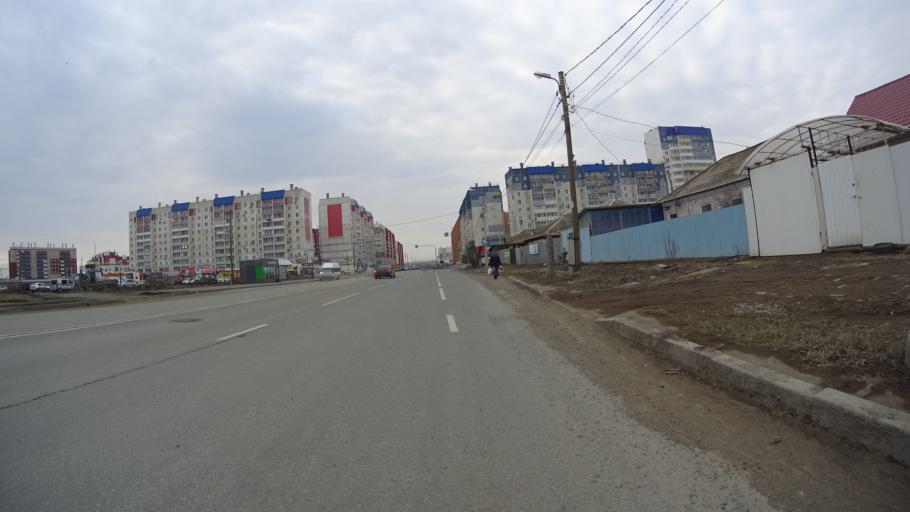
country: RU
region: Chelyabinsk
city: Zheleznodorozhnyy
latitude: 55.1656
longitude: 61.5223
